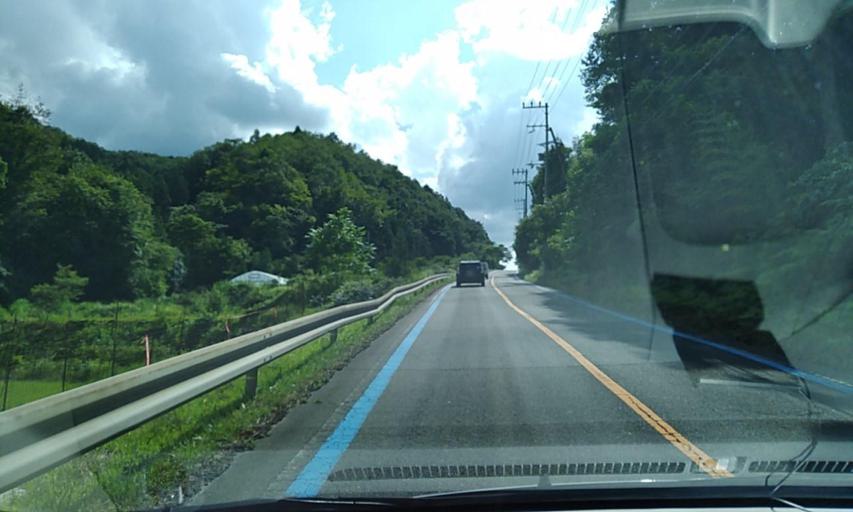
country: JP
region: Kyoto
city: Ayabe
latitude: 35.3162
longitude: 135.3112
